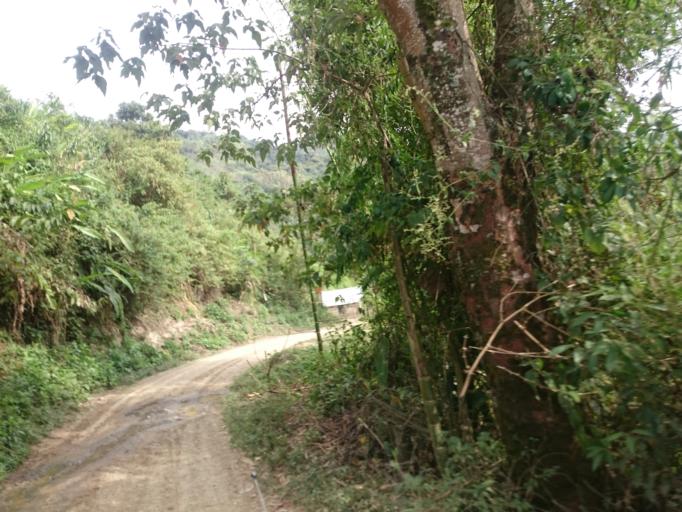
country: CO
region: Cauca
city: Suarez
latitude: 2.9328
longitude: -76.7189
